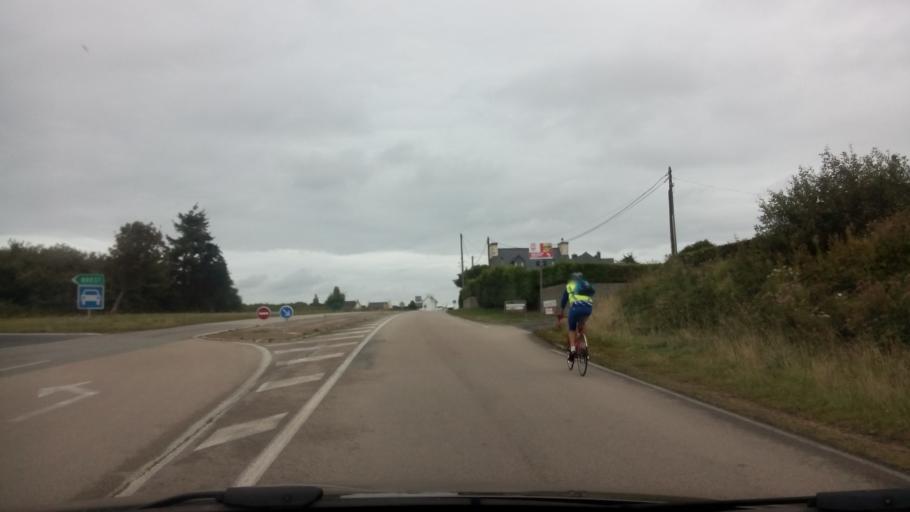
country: FR
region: Brittany
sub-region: Departement du Finistere
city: Morlaix
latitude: 48.5937
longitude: -3.8193
